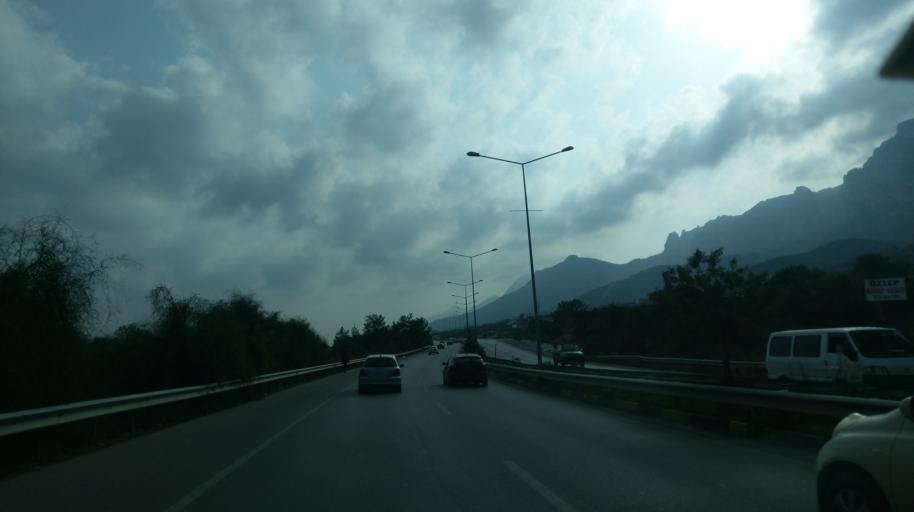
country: CY
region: Keryneia
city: Kyrenia
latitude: 35.3339
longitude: 33.2662
